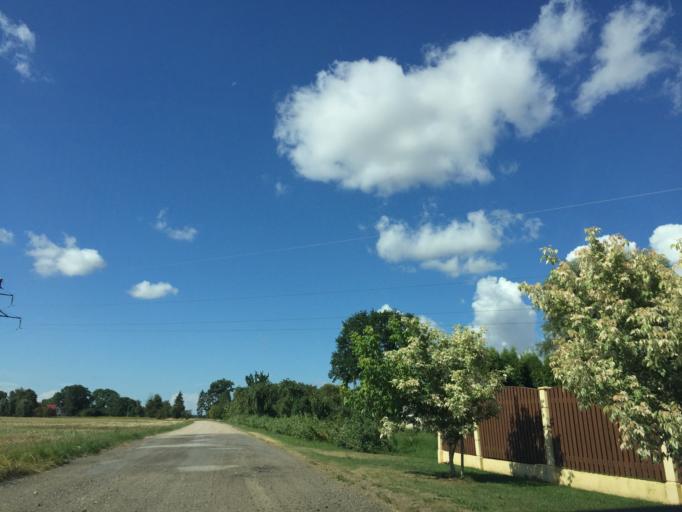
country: LV
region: Bauskas Rajons
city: Bauska
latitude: 56.4236
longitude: 24.1810
